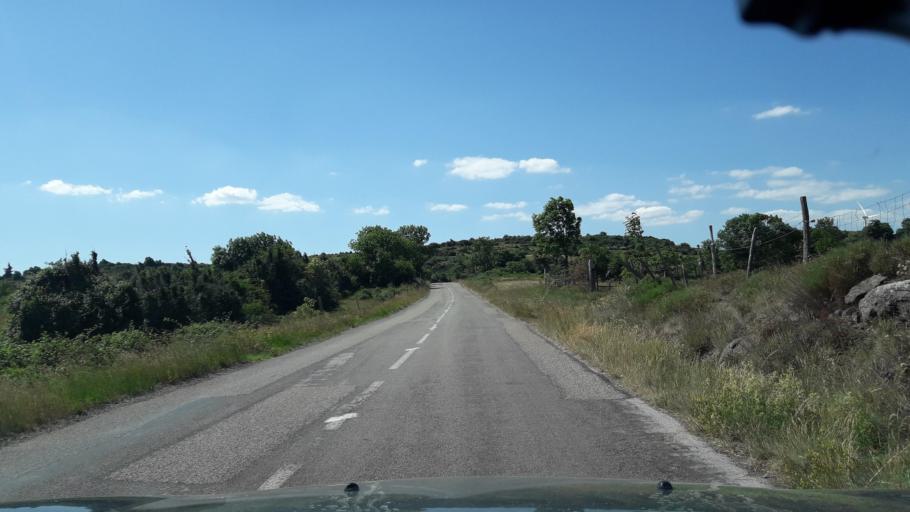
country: FR
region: Rhone-Alpes
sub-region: Departement de l'Ardeche
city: Saint-Priest
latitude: 44.6664
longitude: 4.5640
